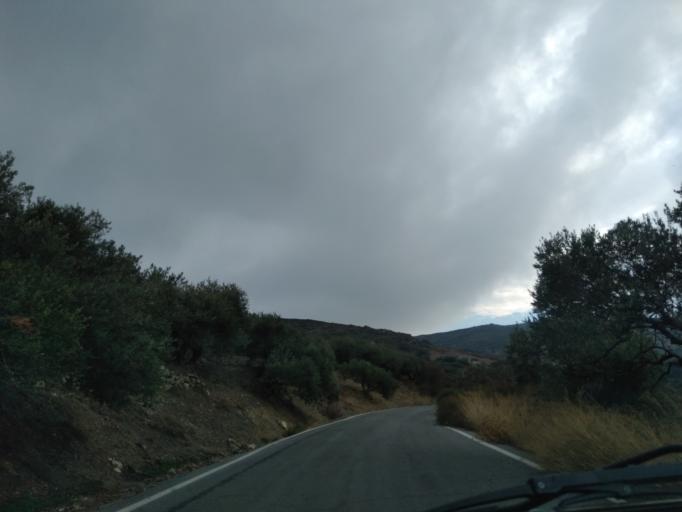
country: GR
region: Crete
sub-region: Nomos Lasithiou
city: Siteia
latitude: 35.1400
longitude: 26.0226
